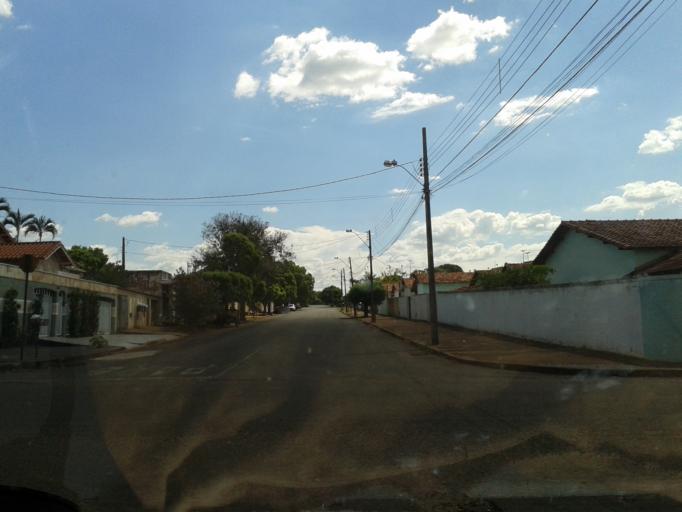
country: BR
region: Minas Gerais
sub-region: Ituiutaba
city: Ituiutaba
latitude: -18.9854
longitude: -49.4518
